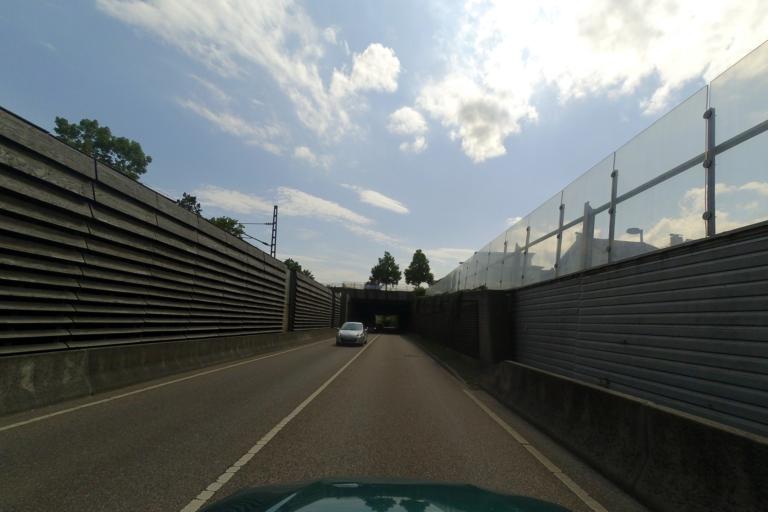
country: DE
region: Baden-Wuerttemberg
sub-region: Regierungsbezirk Stuttgart
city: Aalen
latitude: 48.8638
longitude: 10.1062
